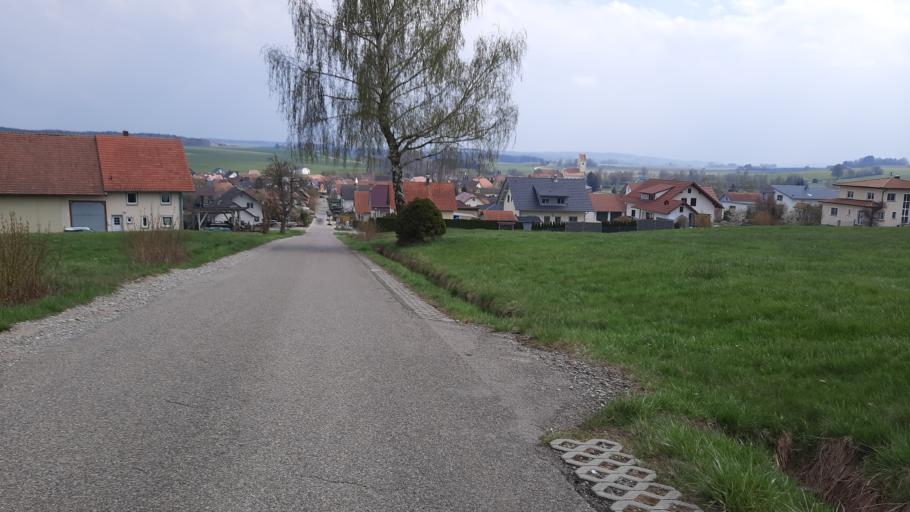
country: DE
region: Baden-Wuerttemberg
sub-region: Tuebingen Region
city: Steinhausen an der Rottum
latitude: 47.9820
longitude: 9.9391
